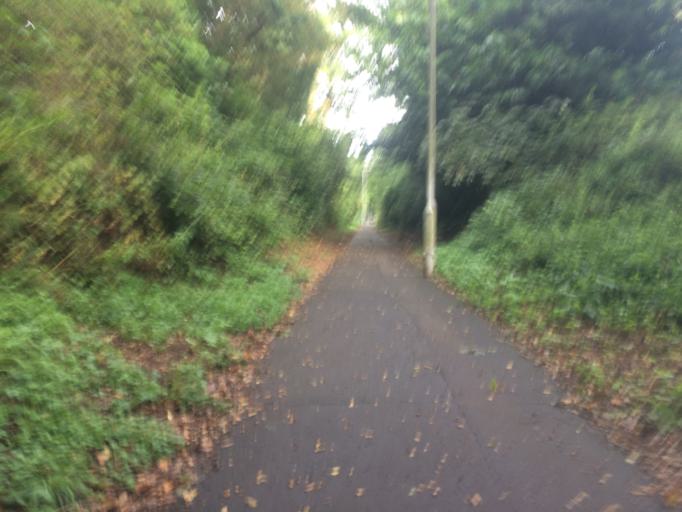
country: GB
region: Scotland
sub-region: Fife
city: Glenrothes
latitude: 56.2033
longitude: -3.1841
